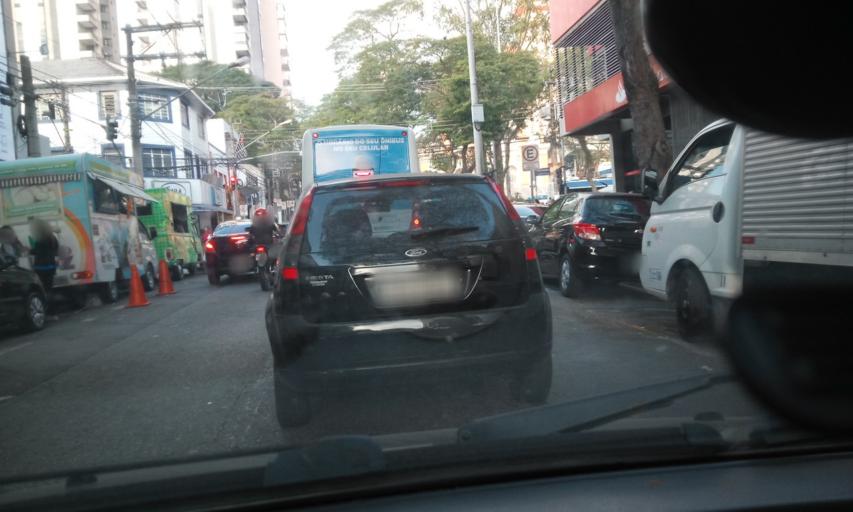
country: BR
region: Sao Paulo
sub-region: Sao Bernardo Do Campo
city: Sao Bernardo do Campo
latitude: -23.7079
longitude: -46.5514
